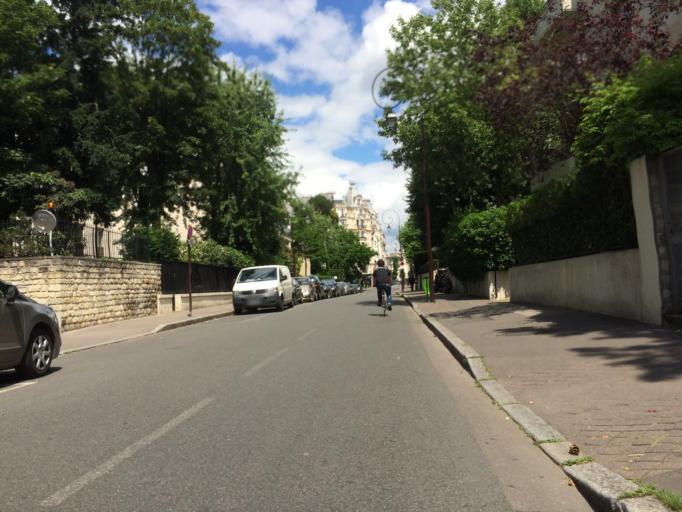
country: FR
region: Ile-de-France
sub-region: Departement des Hauts-de-Seine
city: Puteaux
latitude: 48.8800
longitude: 2.2536
